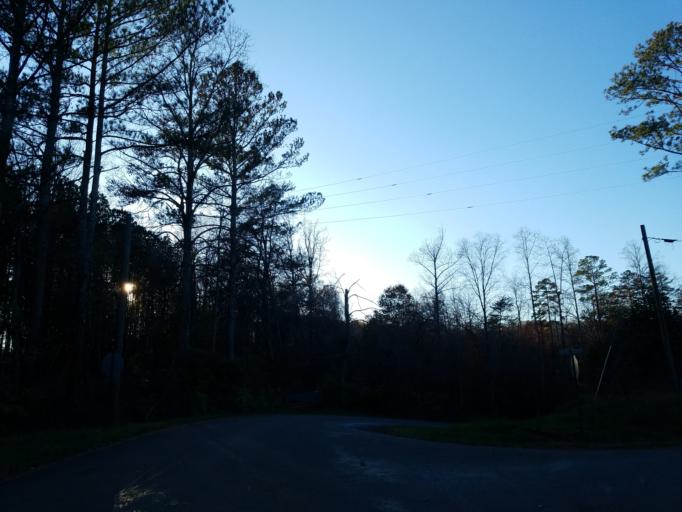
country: US
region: Georgia
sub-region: Pickens County
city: Nelson
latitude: 34.4015
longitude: -84.3764
